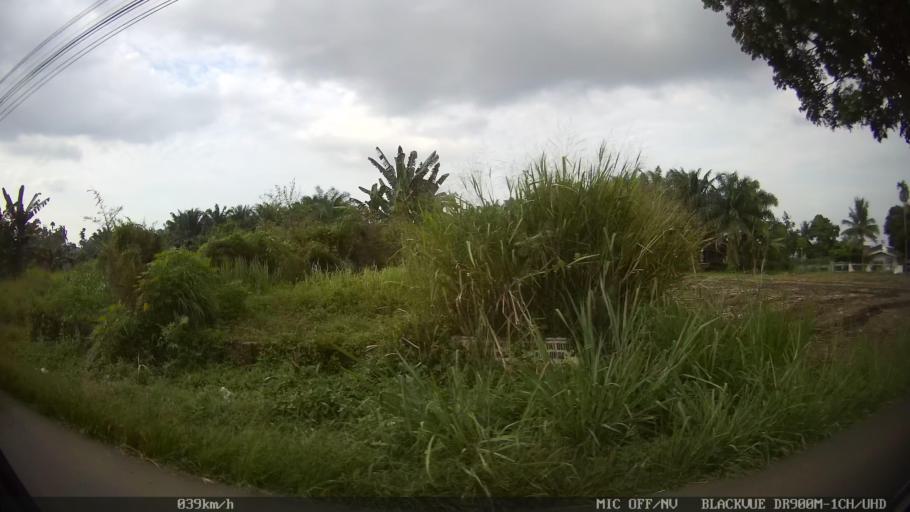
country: ID
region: North Sumatra
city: Sunggal
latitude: 3.5283
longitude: 98.6093
